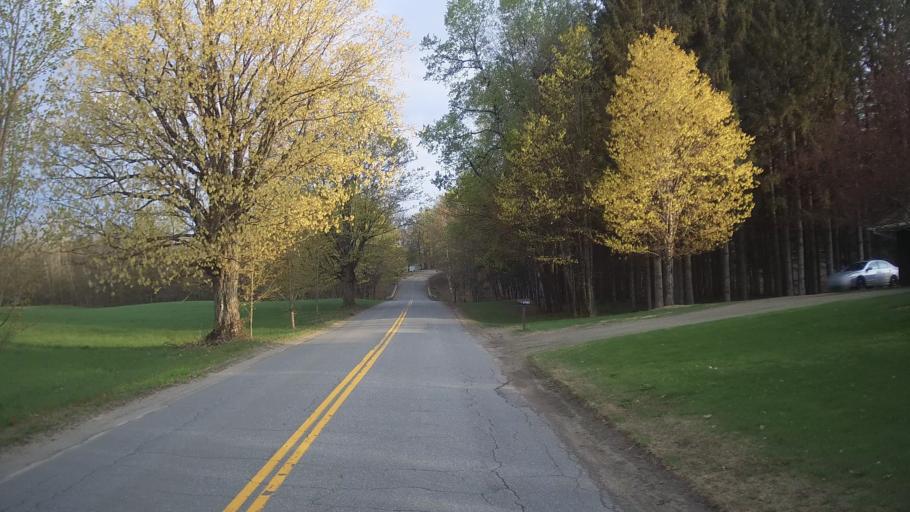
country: US
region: Vermont
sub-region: Orleans County
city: Newport
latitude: 44.9141
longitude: -72.4306
